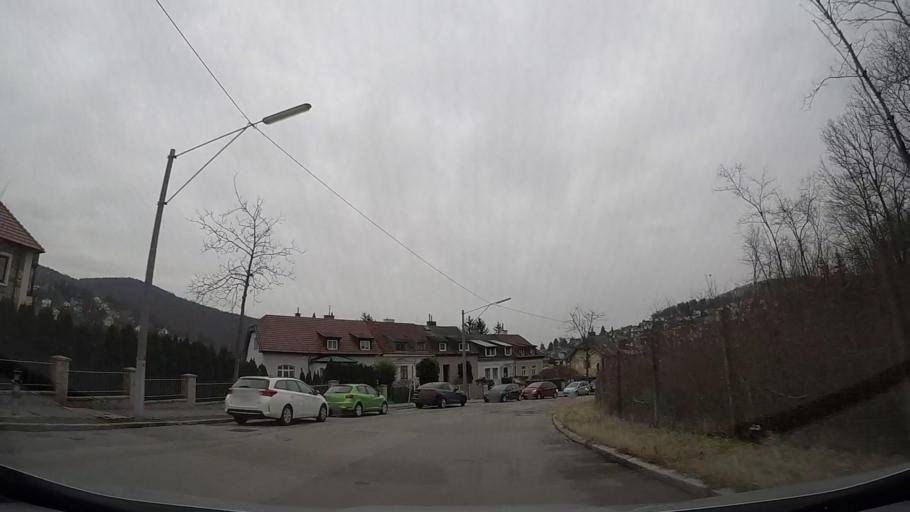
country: AT
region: Lower Austria
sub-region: Politischer Bezirk Wien-Umgebung
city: Purkersdorf
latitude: 48.2156
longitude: 16.2458
